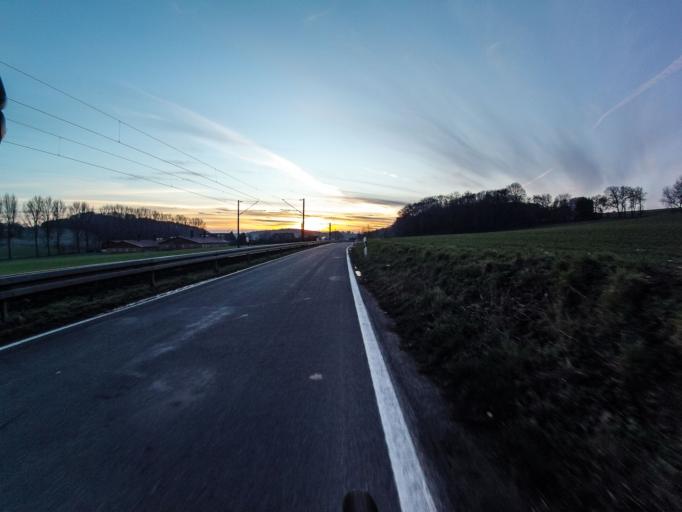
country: DE
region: North Rhine-Westphalia
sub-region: Regierungsbezirk Munster
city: Tecklenburg
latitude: 52.2624
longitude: 7.8259
